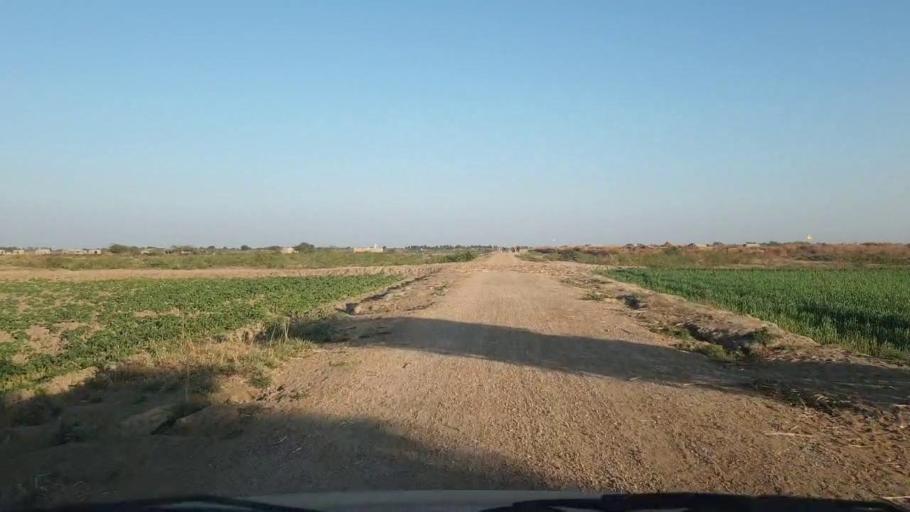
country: PK
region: Sindh
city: Samaro
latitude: 25.3224
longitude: 69.2901
